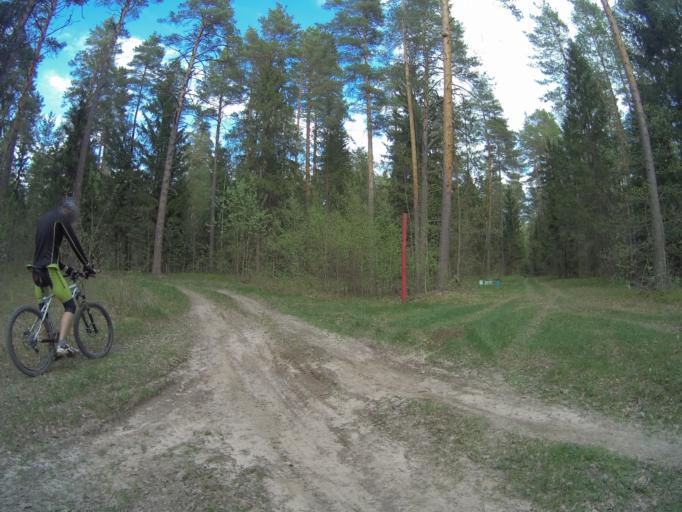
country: RU
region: Vladimir
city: Orgtrud
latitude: 56.1176
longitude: 40.7172
